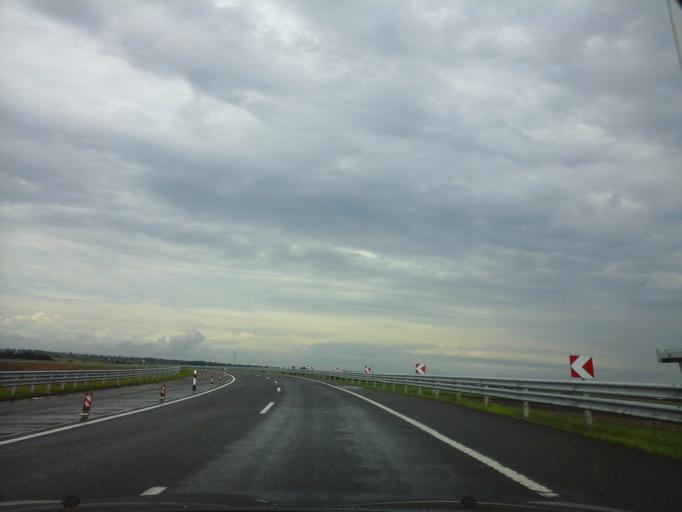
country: HU
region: Hajdu-Bihar
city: Gorbehaza
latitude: 47.7937
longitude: 21.2548
